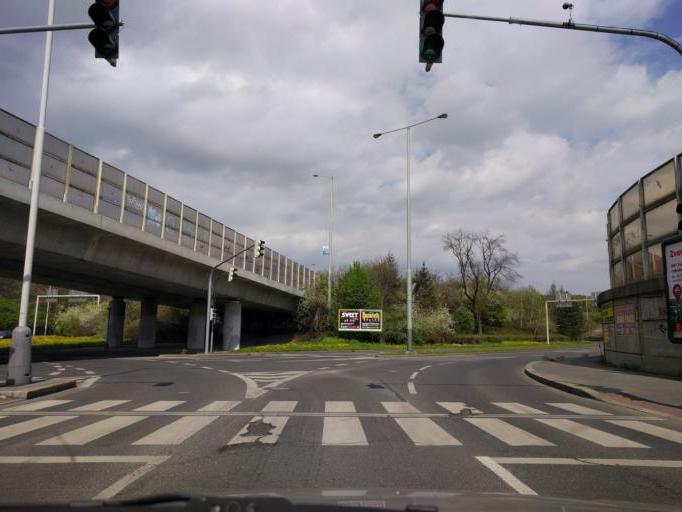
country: CZ
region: Praha
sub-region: Praha 8
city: Liben
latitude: 50.1057
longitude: 14.4818
